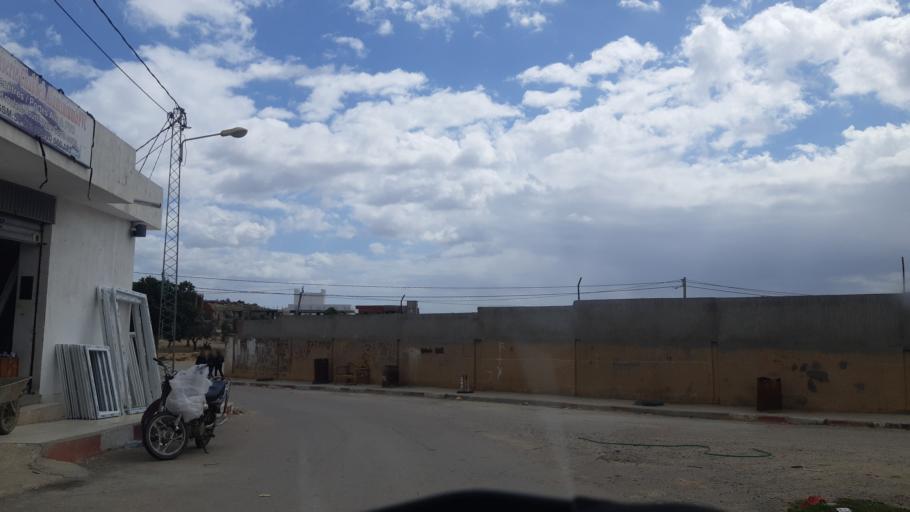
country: TN
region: Susah
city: Akouda
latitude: 35.8611
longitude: 10.5372
